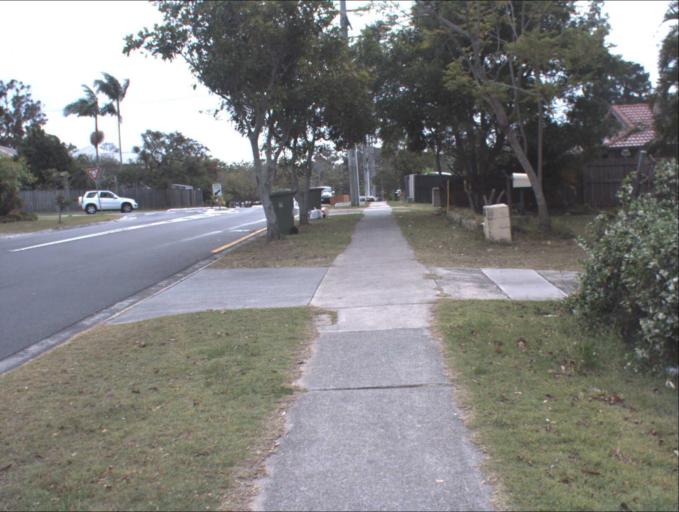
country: AU
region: Queensland
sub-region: Logan
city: Logan City
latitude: -27.6322
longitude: 153.1216
